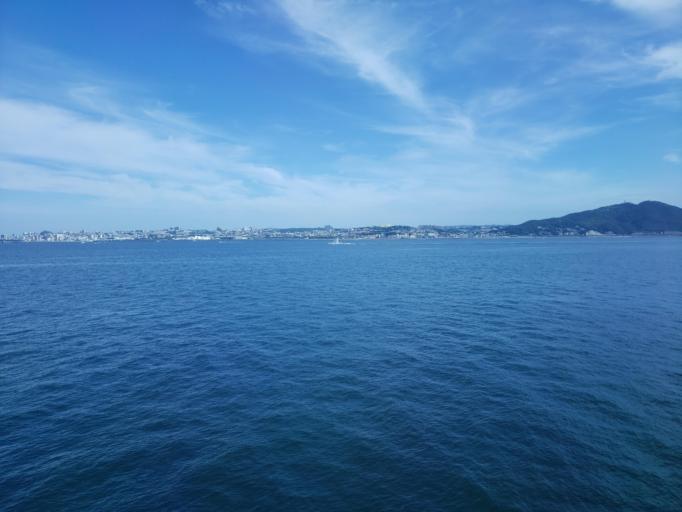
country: JP
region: Hyogo
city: Akashi
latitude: 34.6023
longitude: 135.0847
